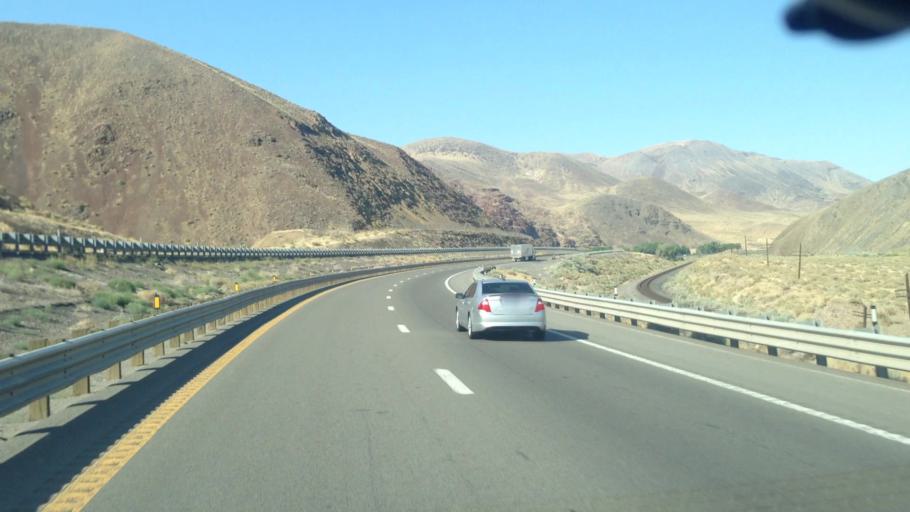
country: US
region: Nevada
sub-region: Lyon County
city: Fernley
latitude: 39.5844
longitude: -119.4683
